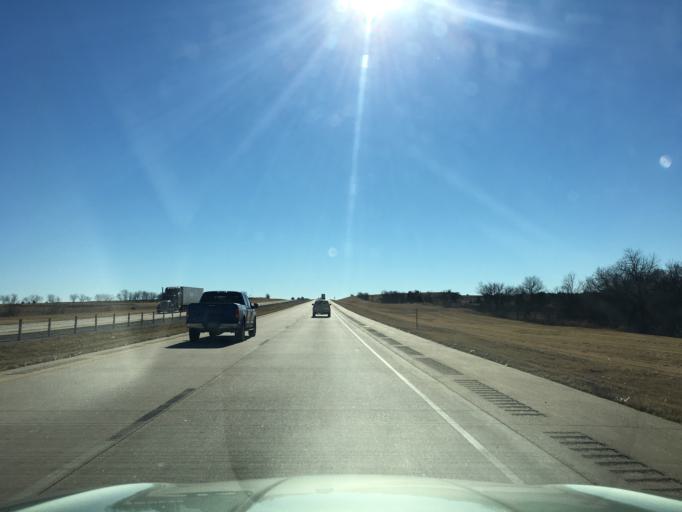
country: US
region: Oklahoma
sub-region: Noble County
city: Perry
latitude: 36.4588
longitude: -97.3271
